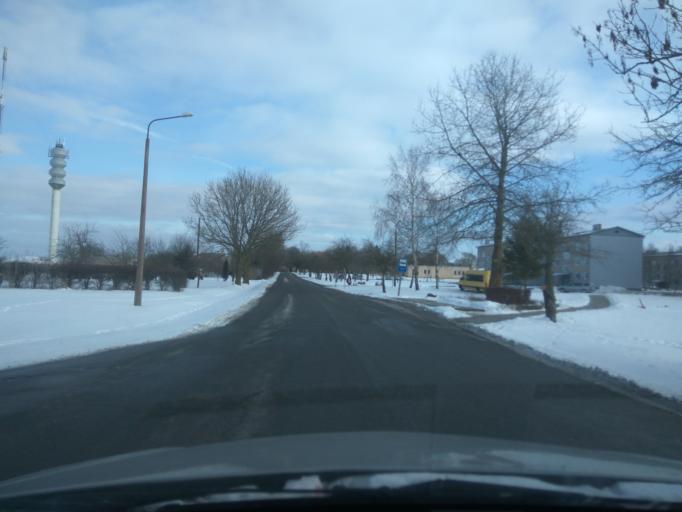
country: LV
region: Ventspils
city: Ventspils
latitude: 57.3327
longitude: 21.6353
